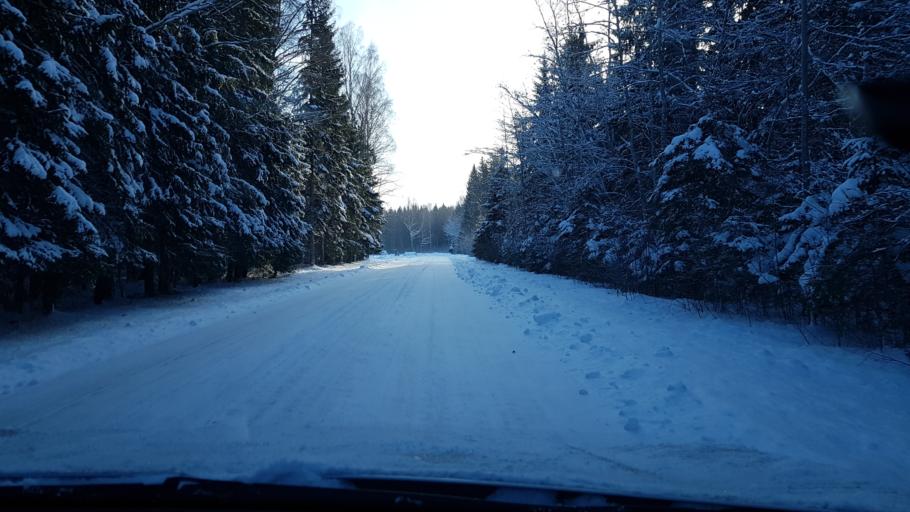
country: EE
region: Harju
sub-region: Nissi vald
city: Turba
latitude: 59.1302
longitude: 24.1965
